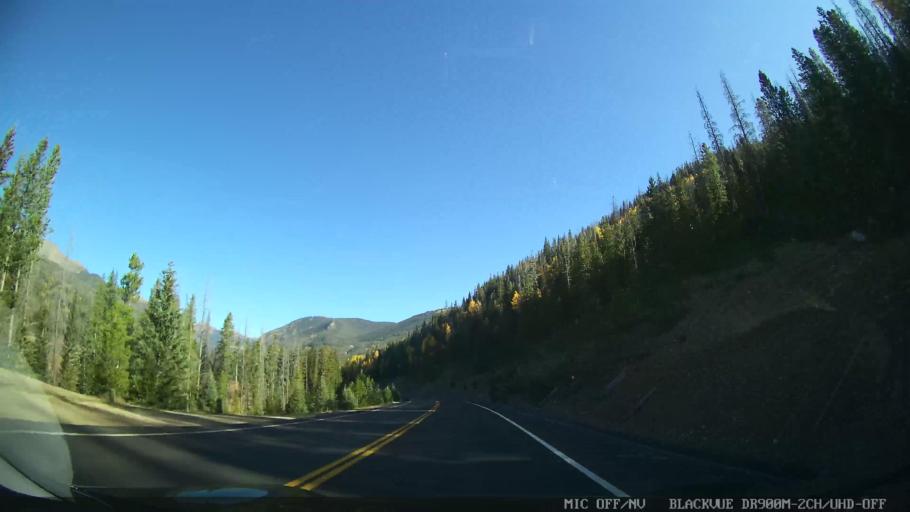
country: US
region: Colorado
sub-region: Grand County
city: Granby
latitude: 40.3832
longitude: -105.8487
